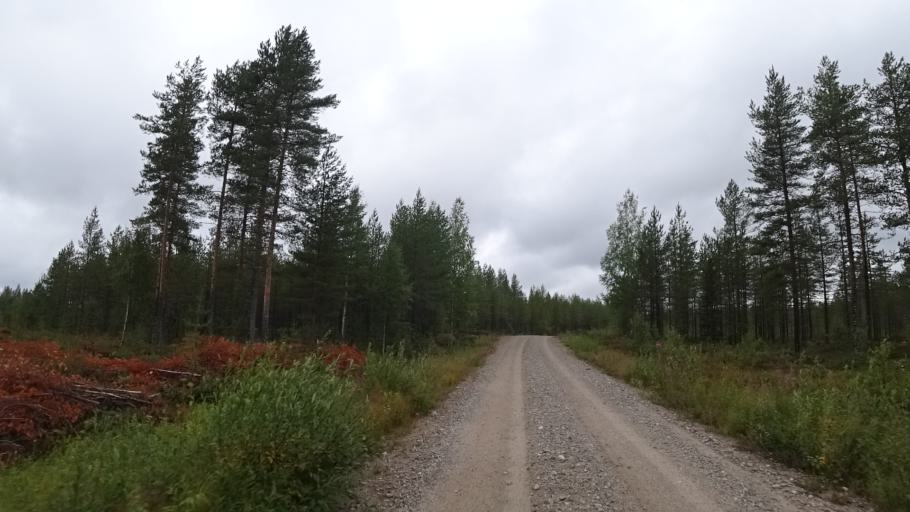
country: FI
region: North Karelia
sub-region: Pielisen Karjala
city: Lieksa
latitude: 63.5132
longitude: 30.1292
